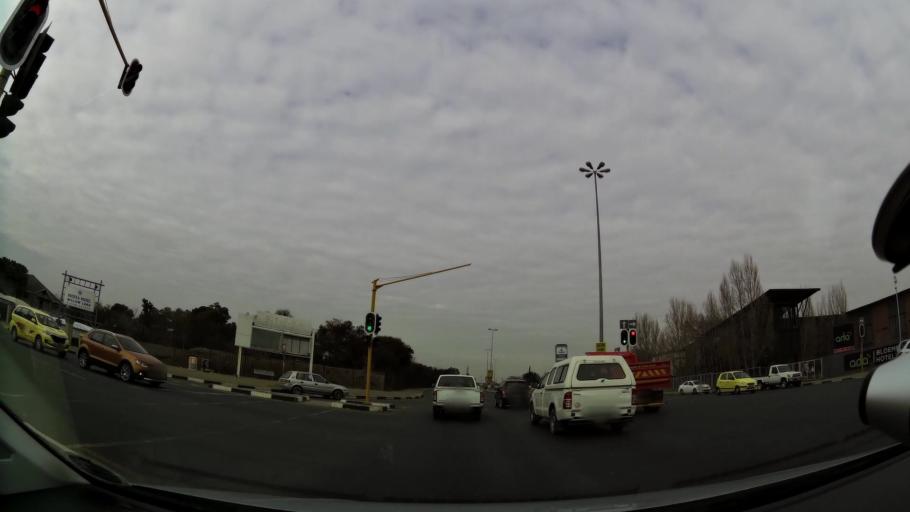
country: ZA
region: Orange Free State
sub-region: Mangaung Metropolitan Municipality
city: Bloemfontein
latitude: -29.1113
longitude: 26.2020
